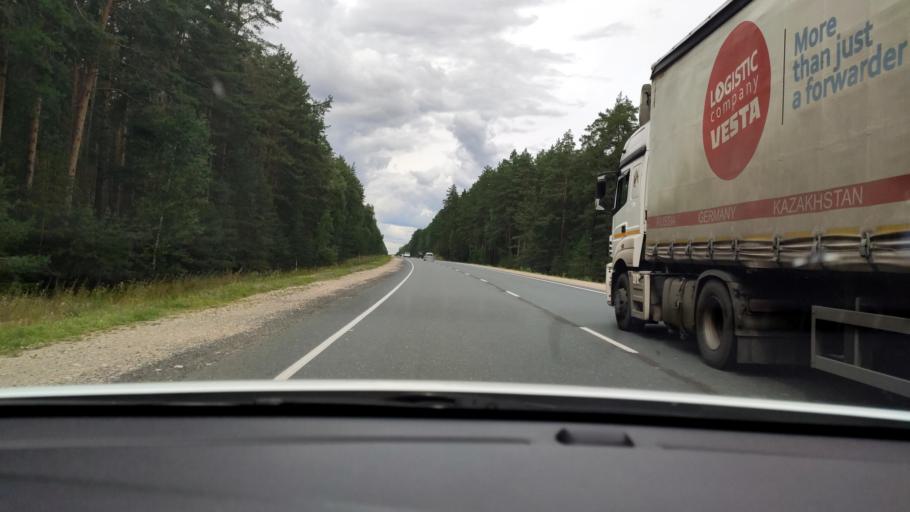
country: RU
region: Mariy-El
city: Pomary
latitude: 56.0308
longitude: 48.3821
